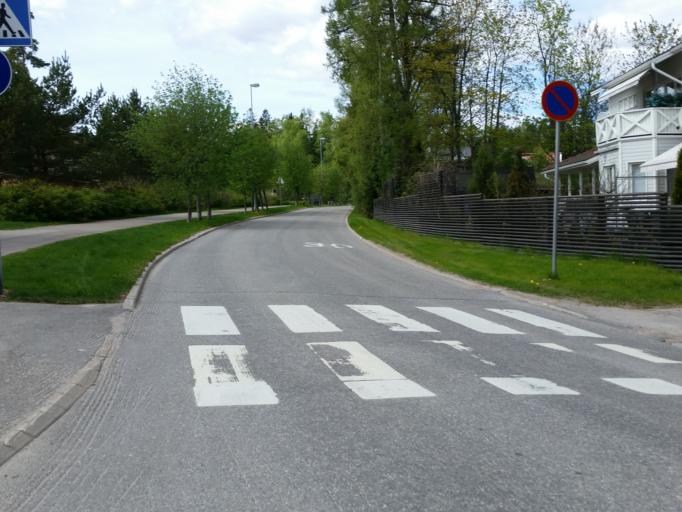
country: FI
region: Uusimaa
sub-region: Helsinki
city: Espoo
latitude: 60.2123
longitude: 24.6408
